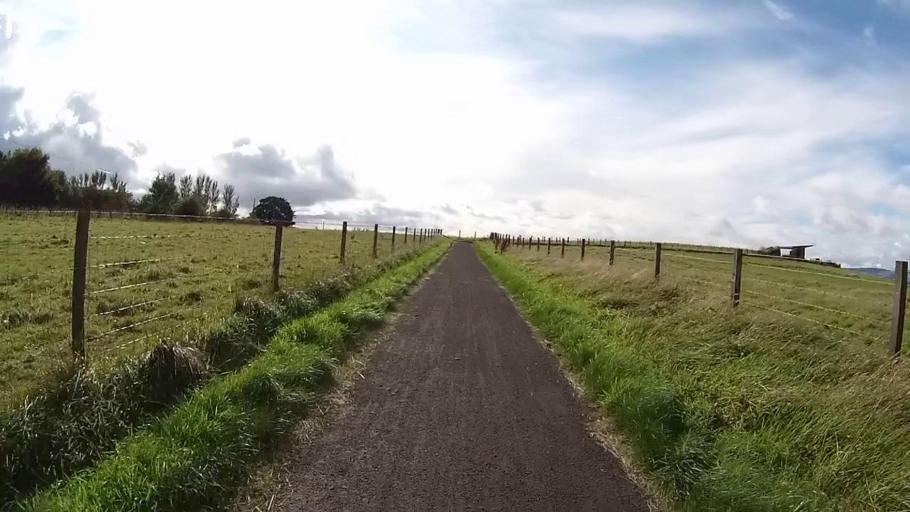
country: GB
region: Scotland
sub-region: Fife
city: Kelty
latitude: 56.1717
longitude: -3.3780
